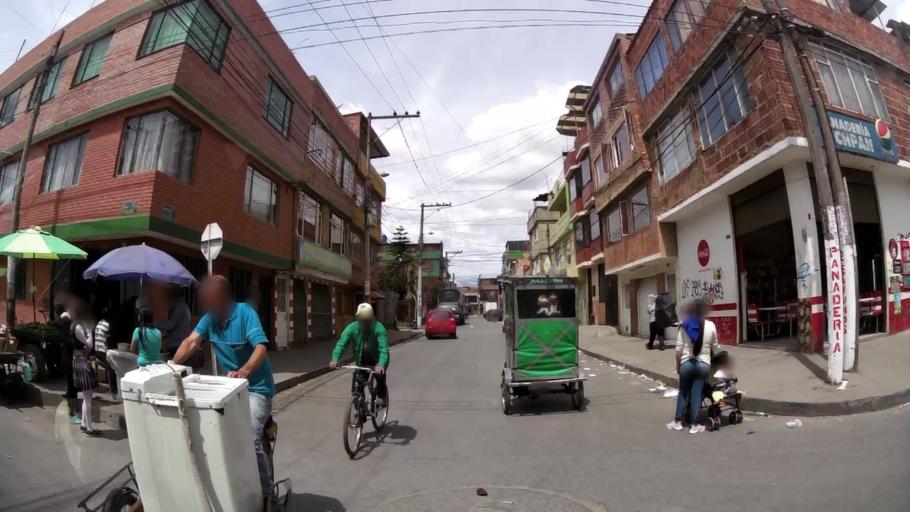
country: CO
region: Cundinamarca
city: Soacha
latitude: 4.6387
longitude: -74.1672
